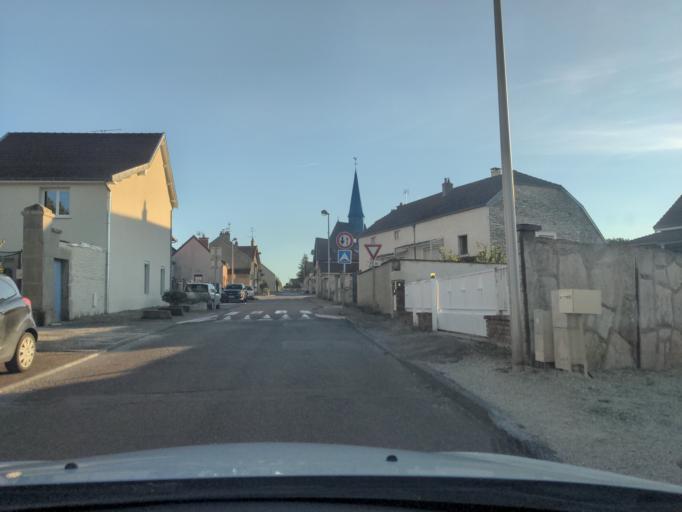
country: FR
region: Bourgogne
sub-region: Departement de la Cote-d'Or
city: Ruffey-les-Echirey
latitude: 47.3804
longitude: 5.0711
